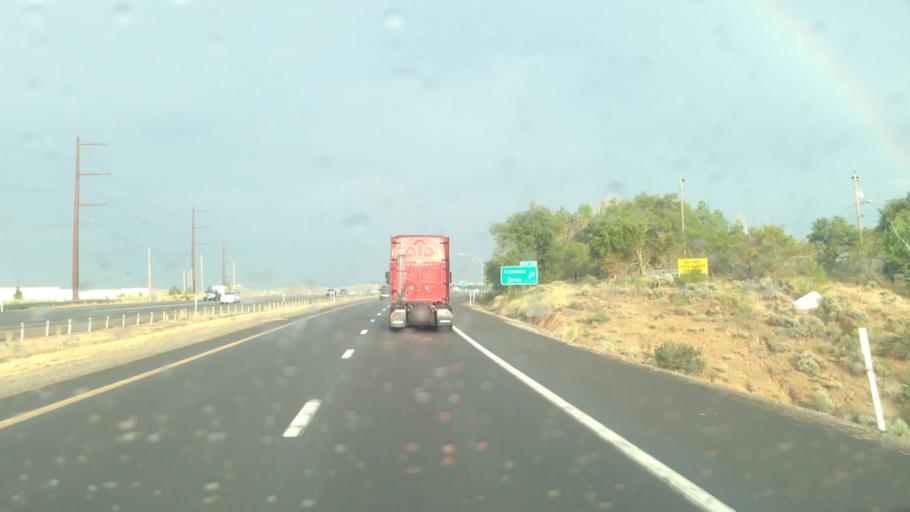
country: US
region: Nevada
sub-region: Washoe County
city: Lemmon Valley
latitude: 39.6134
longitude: -119.8574
